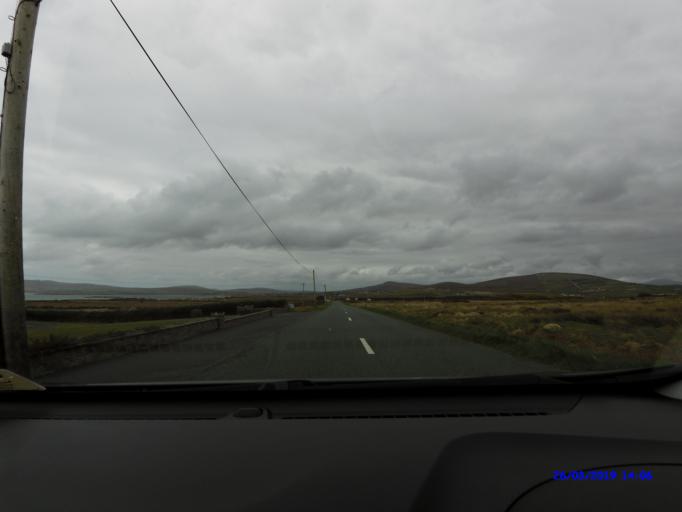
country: IE
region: Connaught
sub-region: Maigh Eo
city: Belmullet
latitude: 54.2070
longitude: -9.9284
